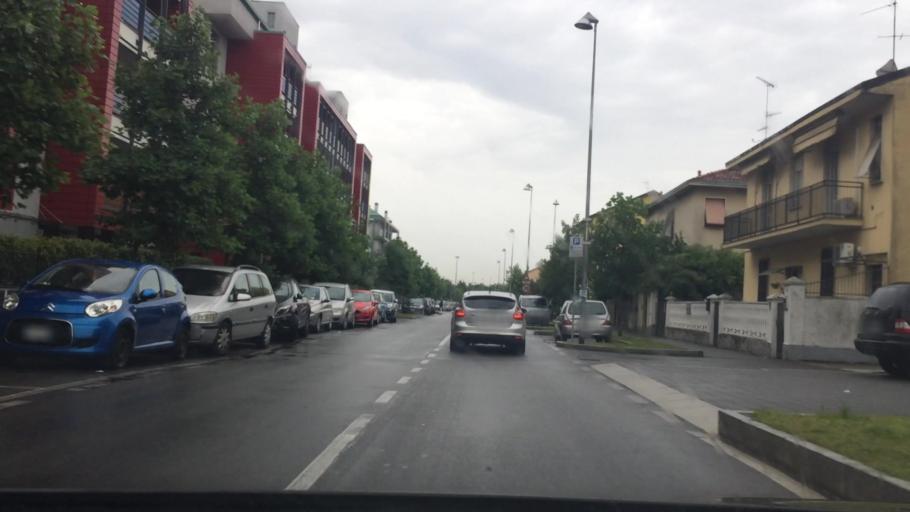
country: IT
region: Lombardy
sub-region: Citta metropolitana di Milano
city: Pero
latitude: 45.5175
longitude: 9.0720
